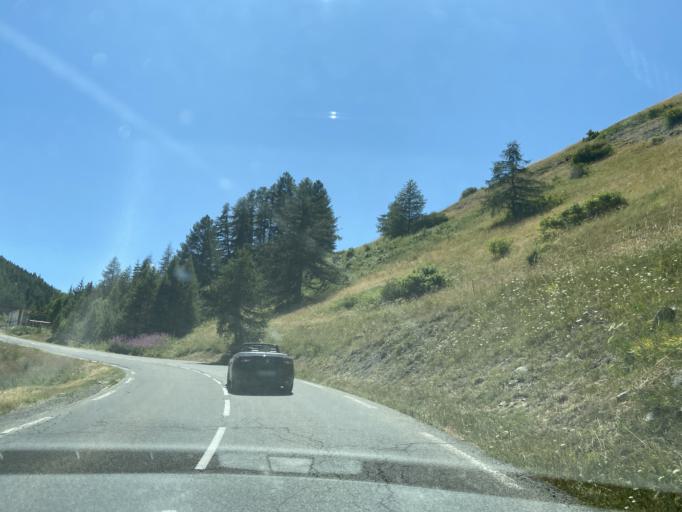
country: FR
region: Provence-Alpes-Cote d'Azur
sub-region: Departement des Hautes-Alpes
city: Guillestre
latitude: 44.5835
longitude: 6.6828
